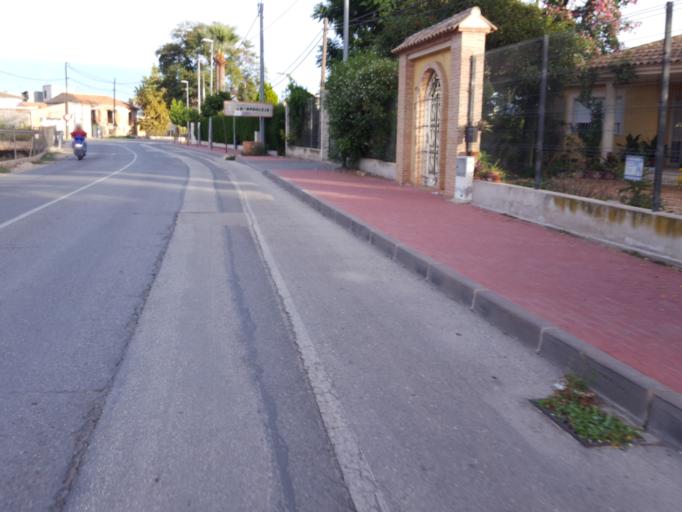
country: ES
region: Murcia
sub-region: Murcia
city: Murcia
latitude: 37.9890
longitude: -1.1640
